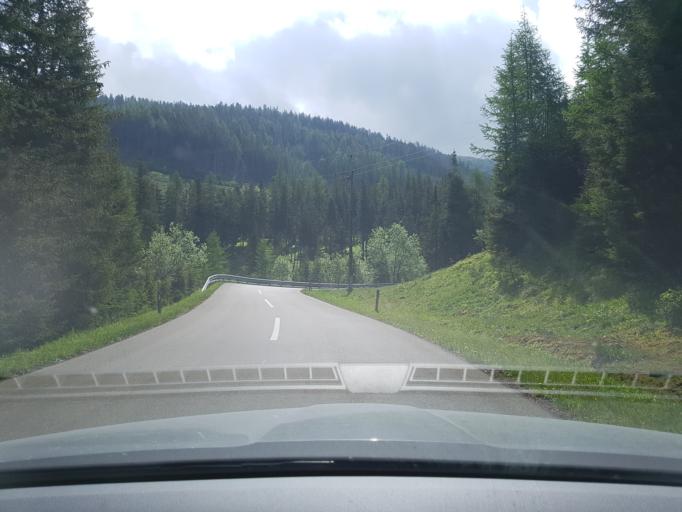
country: AT
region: Salzburg
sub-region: Politischer Bezirk Tamsweg
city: Thomatal
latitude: 46.9560
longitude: 13.7285
